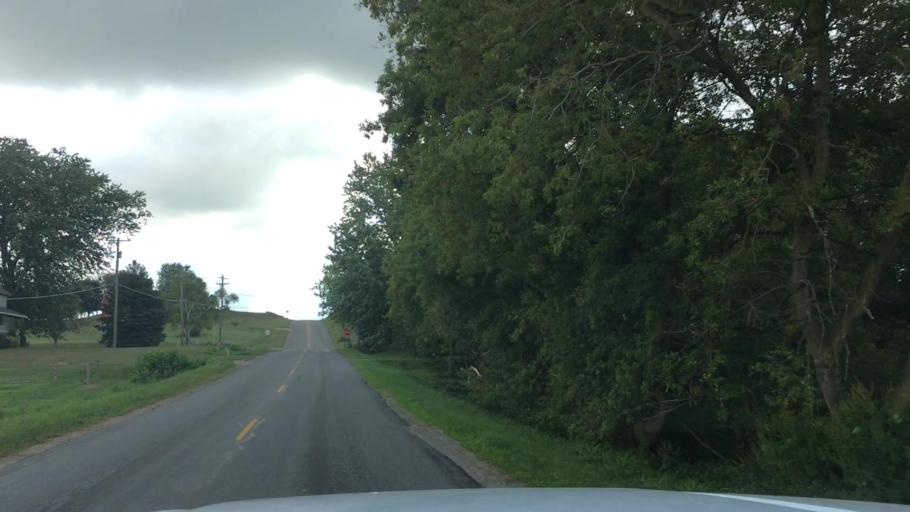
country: US
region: Michigan
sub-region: Ottawa County
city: Hudsonville
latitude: 42.7966
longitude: -85.8434
